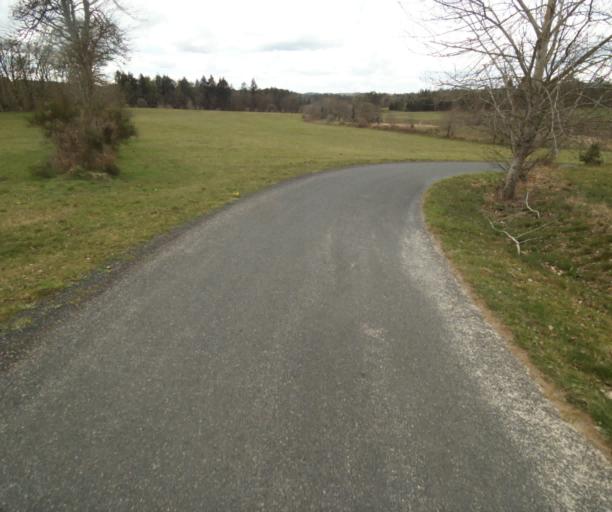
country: FR
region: Limousin
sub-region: Departement de la Correze
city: Correze
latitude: 45.3126
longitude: 1.9296
